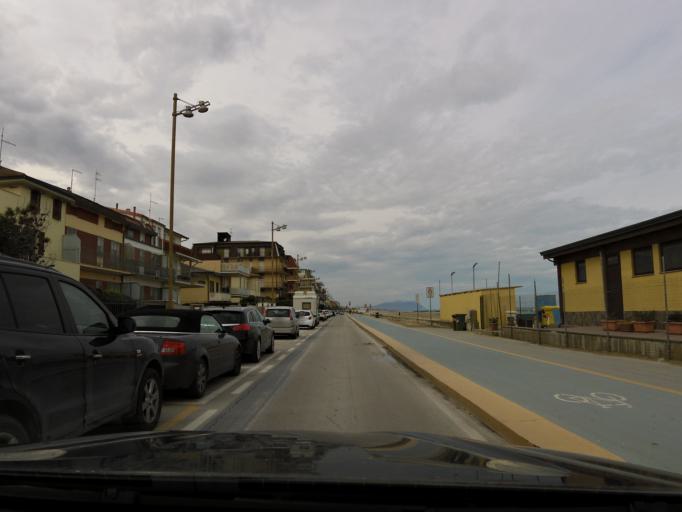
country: IT
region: The Marches
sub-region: Provincia di Macerata
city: Civitanova Marche
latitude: 43.3222
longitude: 13.7190
